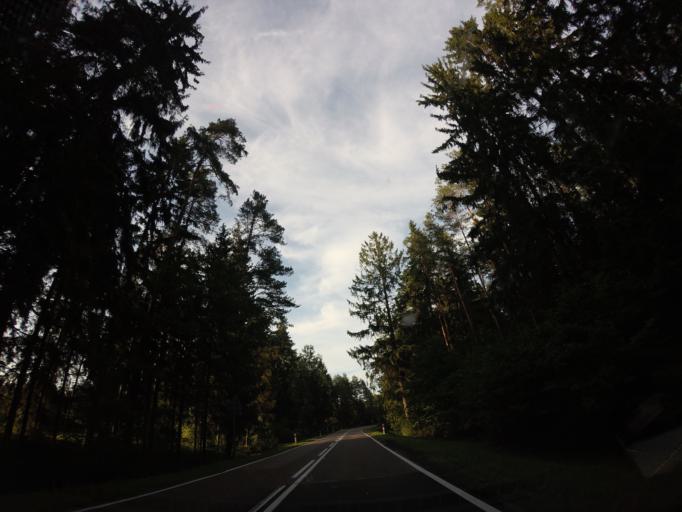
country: PL
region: Podlasie
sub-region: Powiat sejnenski
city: Krasnopol
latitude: 53.9365
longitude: 23.1695
